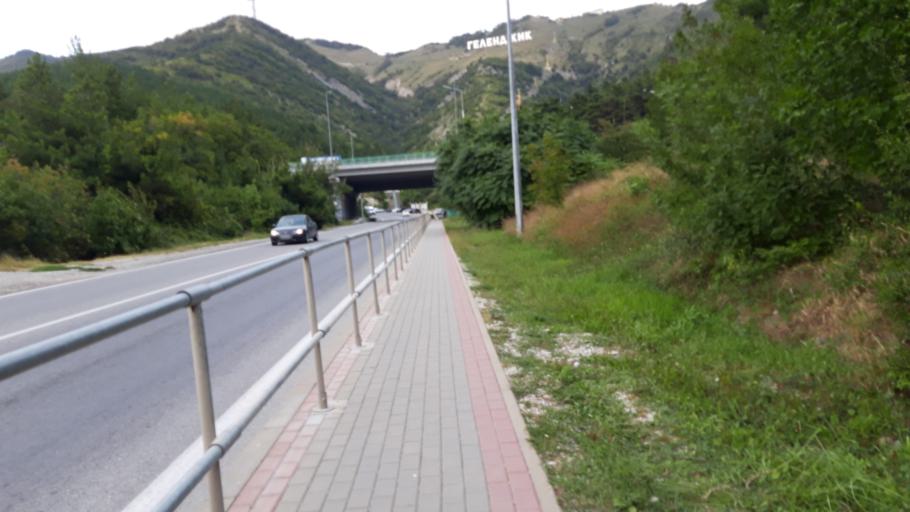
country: RU
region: Krasnodarskiy
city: Gelendzhik
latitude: 44.5747
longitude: 38.0917
